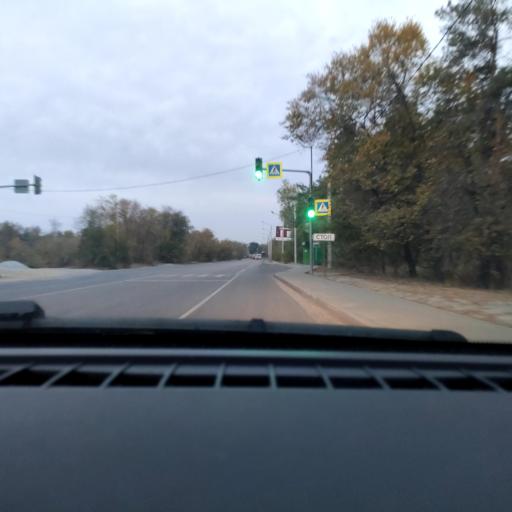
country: RU
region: Voronezj
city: Maslovka
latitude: 51.6342
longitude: 39.2897
